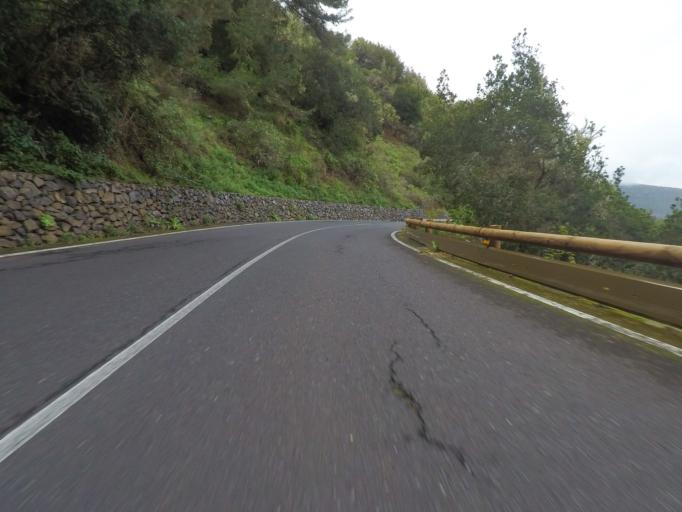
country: ES
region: Canary Islands
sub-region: Provincia de Santa Cruz de Tenerife
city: Hermigua
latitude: 28.1360
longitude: -17.1971
